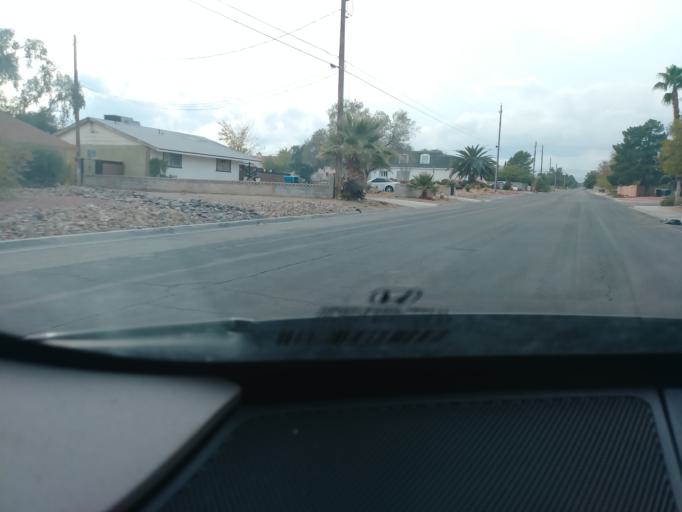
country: US
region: Nevada
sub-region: Clark County
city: Spring Valley
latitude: 36.1405
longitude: -115.2445
